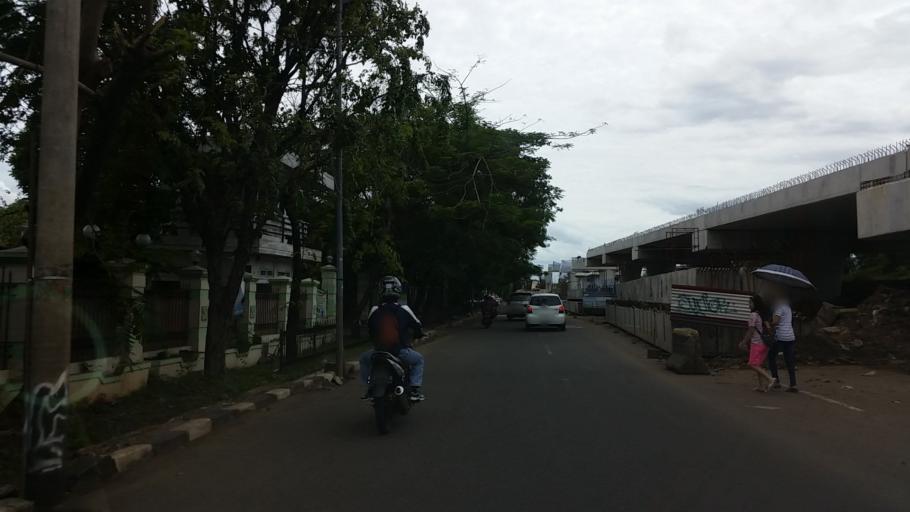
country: ID
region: Jakarta Raya
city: Jakarta
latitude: -6.1147
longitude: 106.7851
